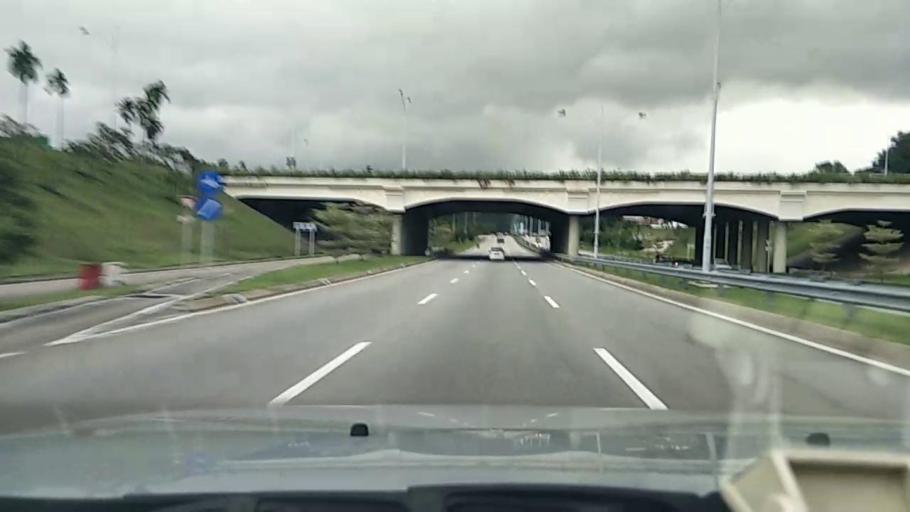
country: MY
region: Putrajaya
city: Putrajaya
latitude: 2.9419
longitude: 101.7142
